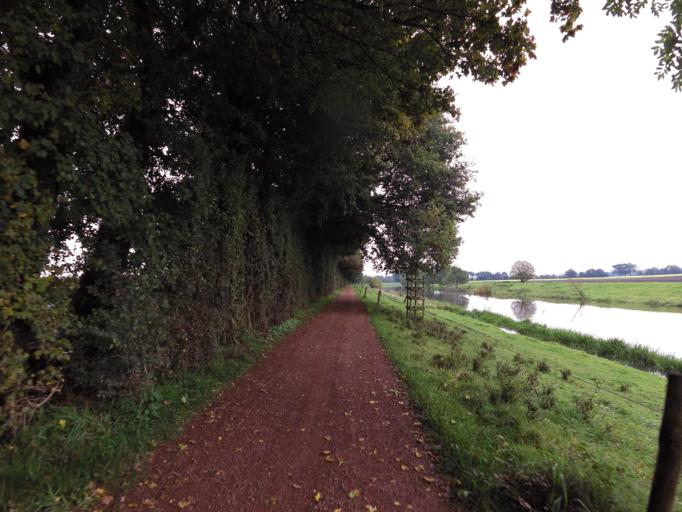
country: DE
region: North Rhine-Westphalia
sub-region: Regierungsbezirk Munster
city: Isselburg
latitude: 51.8490
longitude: 6.5367
